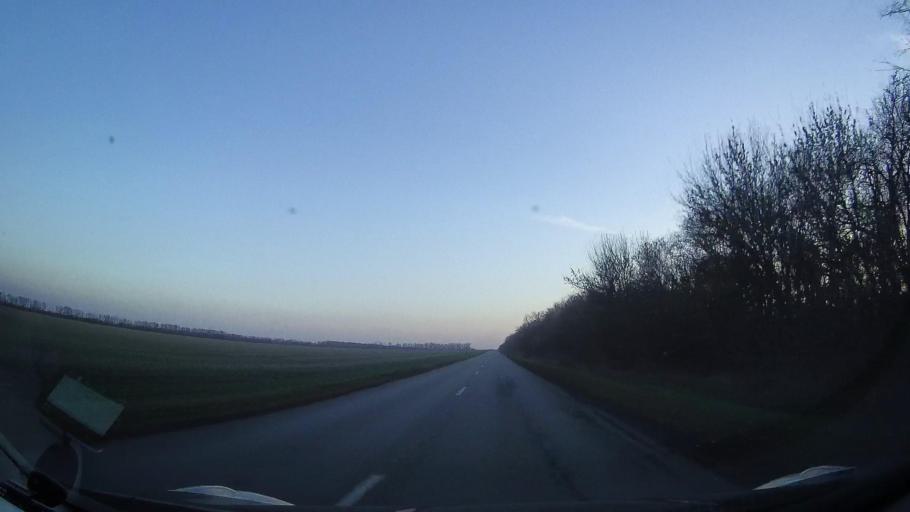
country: RU
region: Rostov
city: Zernograd
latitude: 47.0381
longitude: 40.3915
